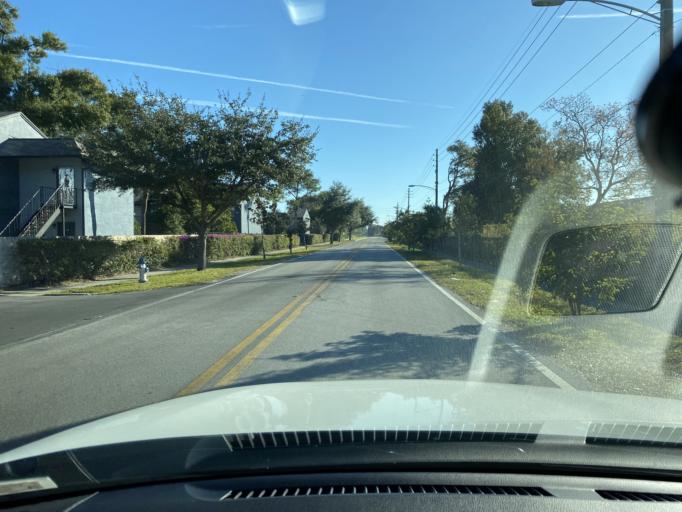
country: US
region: Florida
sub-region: Orange County
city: Azalea Park
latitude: 28.5318
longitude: -81.3061
